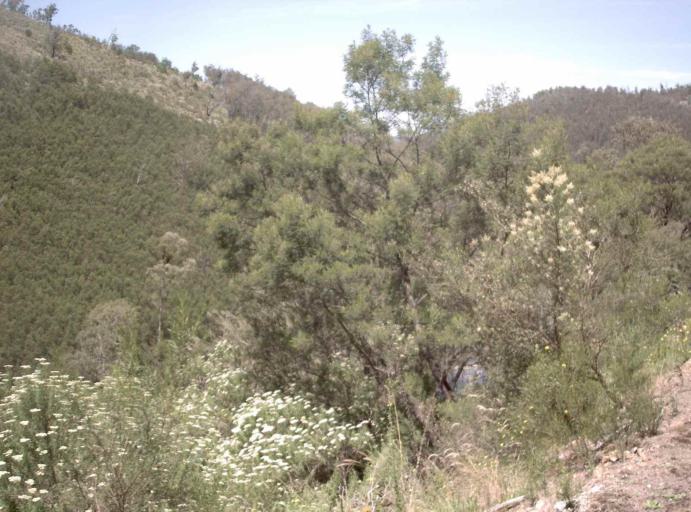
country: AU
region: Victoria
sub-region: East Gippsland
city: Bairnsdale
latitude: -37.4774
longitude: 147.8309
